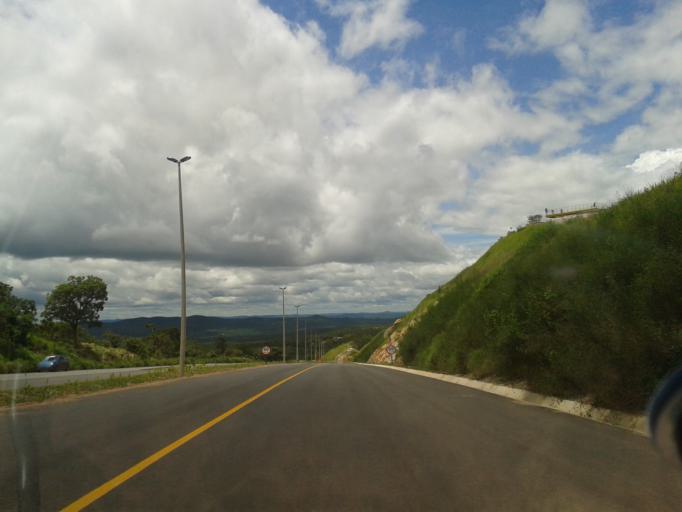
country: BR
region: Goias
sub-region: Goias
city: Goias
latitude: -15.9810
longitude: -50.0885
